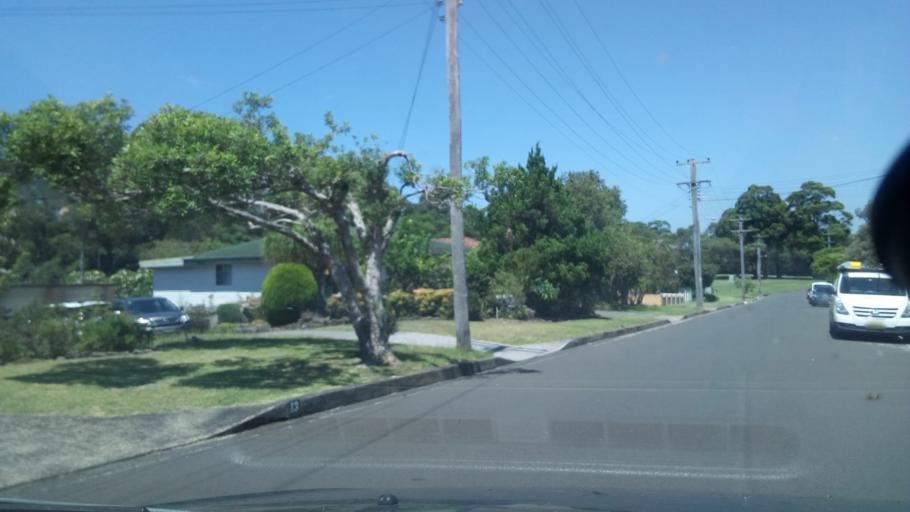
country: AU
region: New South Wales
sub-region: Wollongong
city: West Wollongong
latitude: -34.4250
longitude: 150.8596
